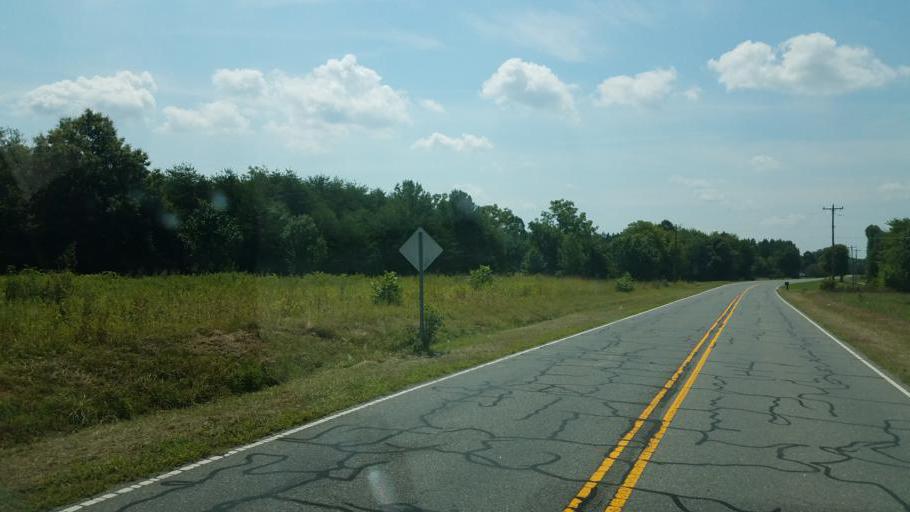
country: US
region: North Carolina
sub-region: Gaston County
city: Cherryville
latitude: 35.4534
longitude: -81.4306
